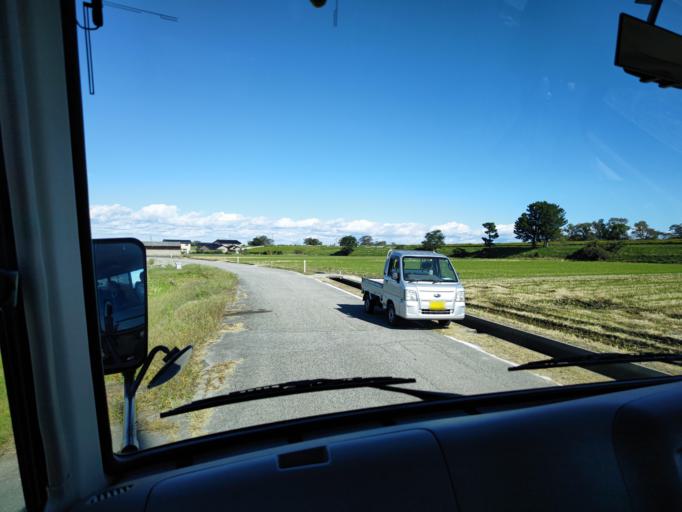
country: JP
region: Toyama
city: Nyuzen
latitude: 36.9091
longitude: 137.4348
